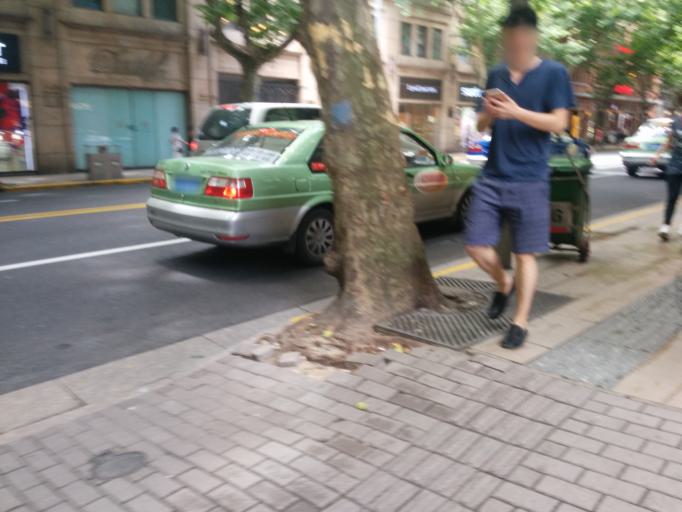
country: CN
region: Shanghai Shi
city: Shanghai
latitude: 31.2203
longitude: 121.4577
